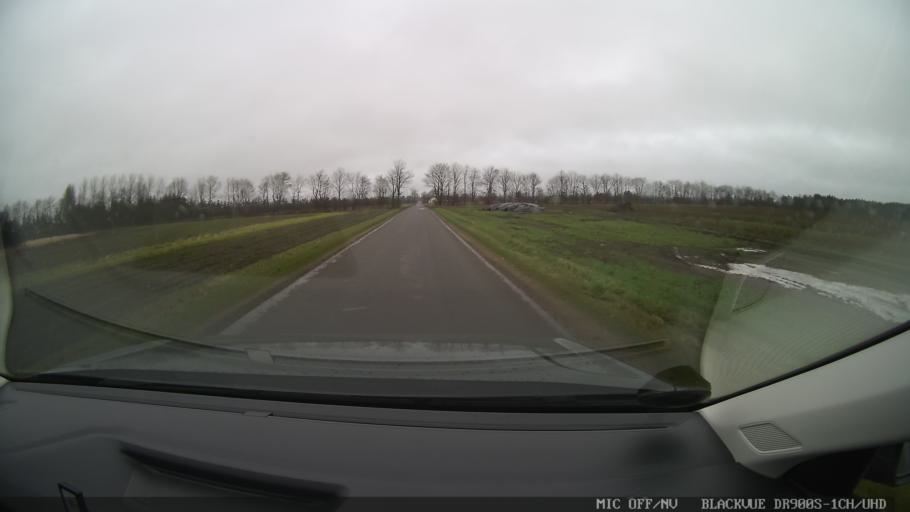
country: DK
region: Central Jutland
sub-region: Viborg Kommune
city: Karup
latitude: 56.3093
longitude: 9.2425
